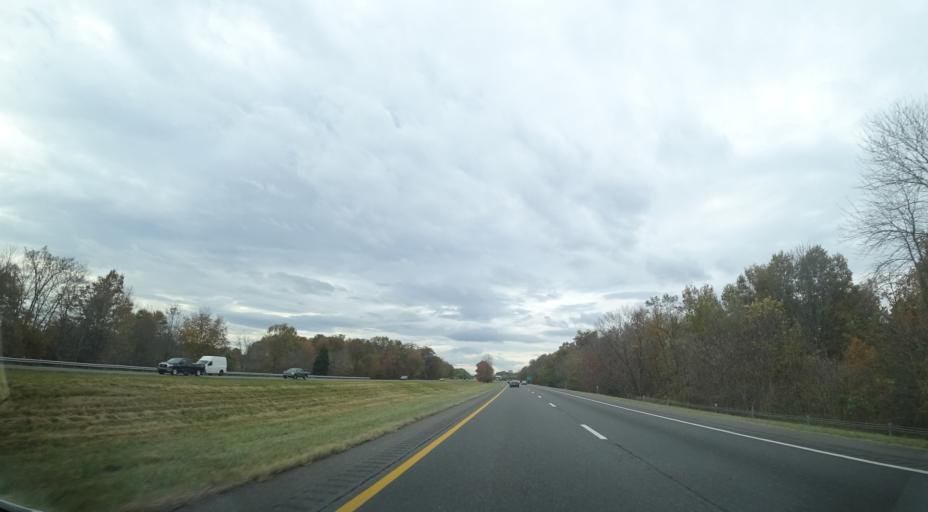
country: US
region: Virginia
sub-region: Fauquier County
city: Marshall
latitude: 38.8587
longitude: -77.8335
